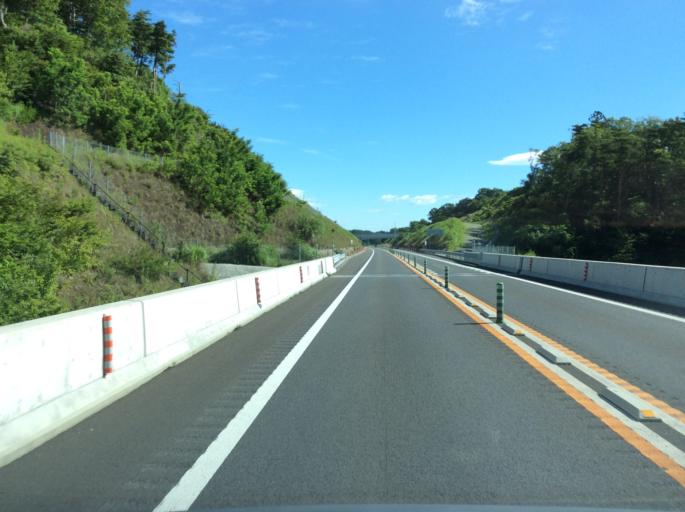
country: JP
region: Fukushima
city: Namie
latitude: 37.4525
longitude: 140.9607
